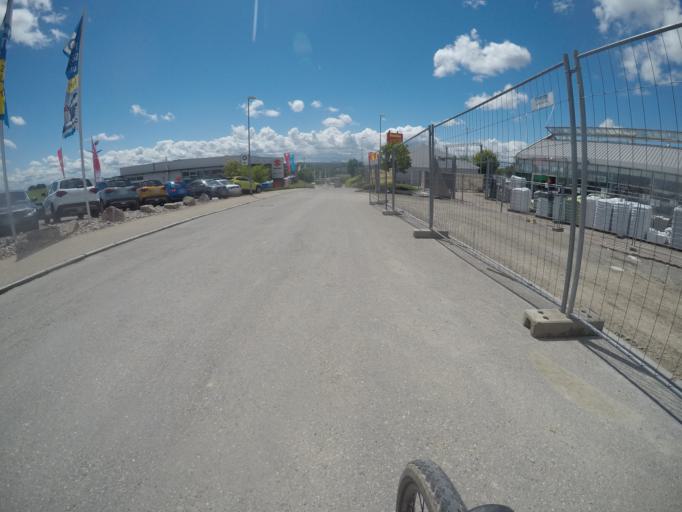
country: DE
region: Baden-Wuerttemberg
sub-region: Karlsruhe Region
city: Horb am Neckar
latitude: 48.4596
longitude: 8.6961
